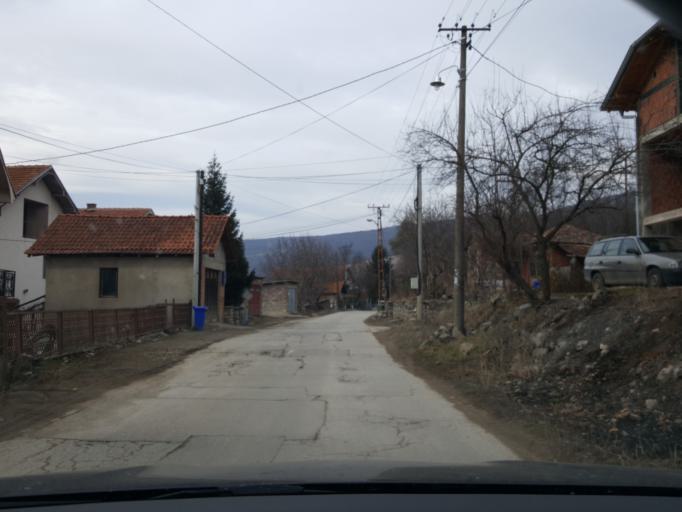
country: RS
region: Central Serbia
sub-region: Pirotski Okrug
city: Dimitrovgrad
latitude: 43.0078
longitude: 22.7591
